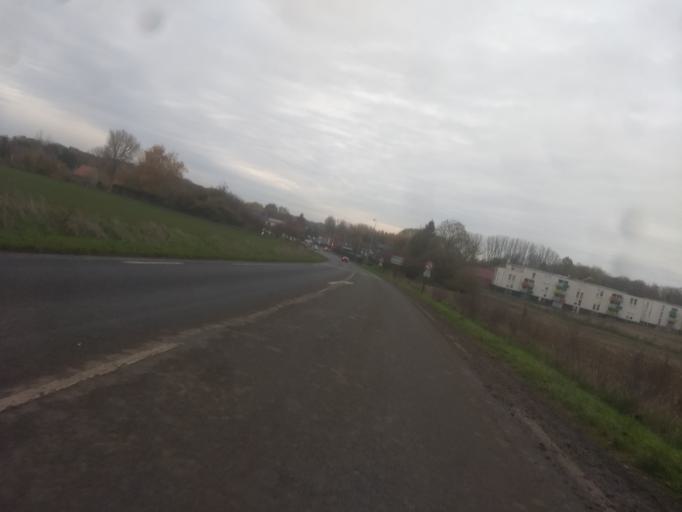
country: FR
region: Nord-Pas-de-Calais
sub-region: Departement du Pas-de-Calais
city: Achicourt
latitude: 50.2682
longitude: 2.7503
